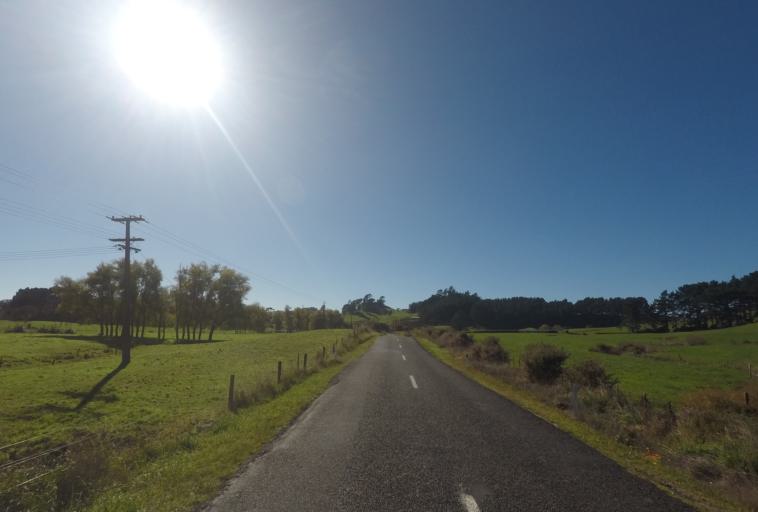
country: NZ
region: Bay of Plenty
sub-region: Western Bay of Plenty District
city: Waihi Beach
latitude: -37.4071
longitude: 175.9010
